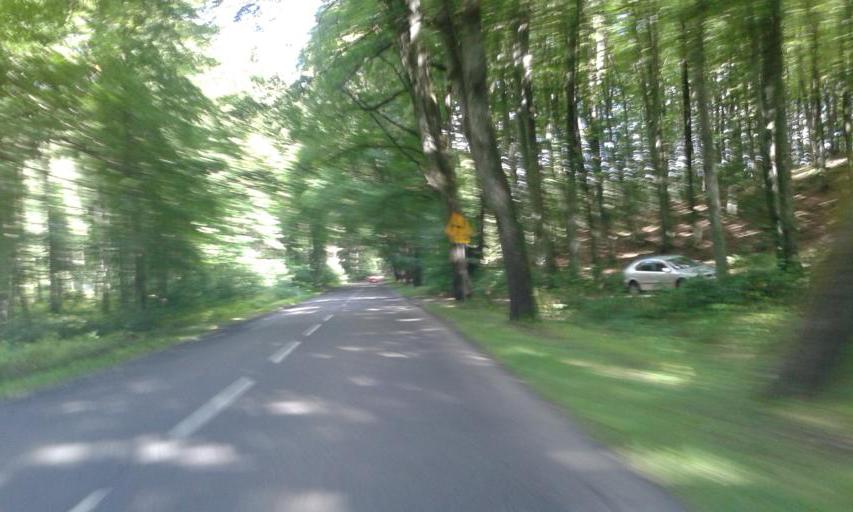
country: PL
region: West Pomeranian Voivodeship
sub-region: Powiat slawienski
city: Slawno
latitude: 54.2640
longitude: 16.6793
